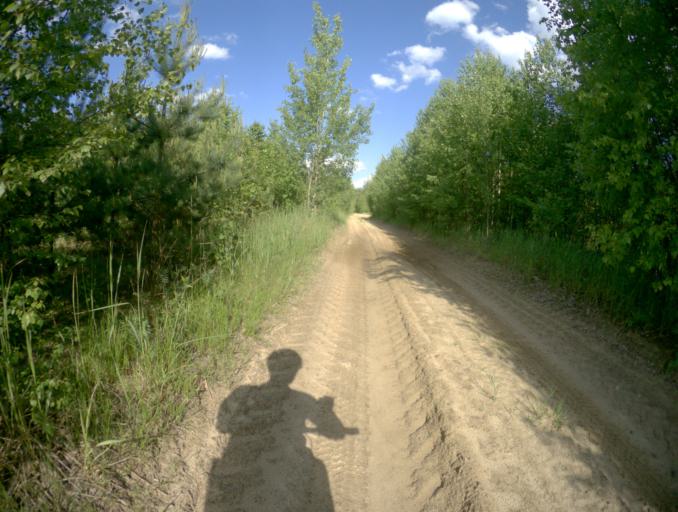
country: RU
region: Vladimir
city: Zolotkovo
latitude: 55.3312
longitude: 40.9961
